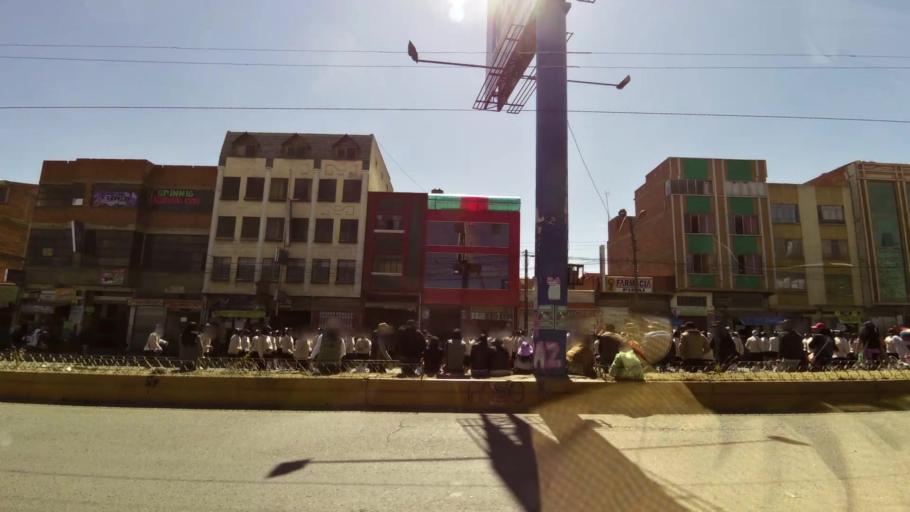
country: BO
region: La Paz
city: La Paz
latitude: -16.4998
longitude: -68.1755
